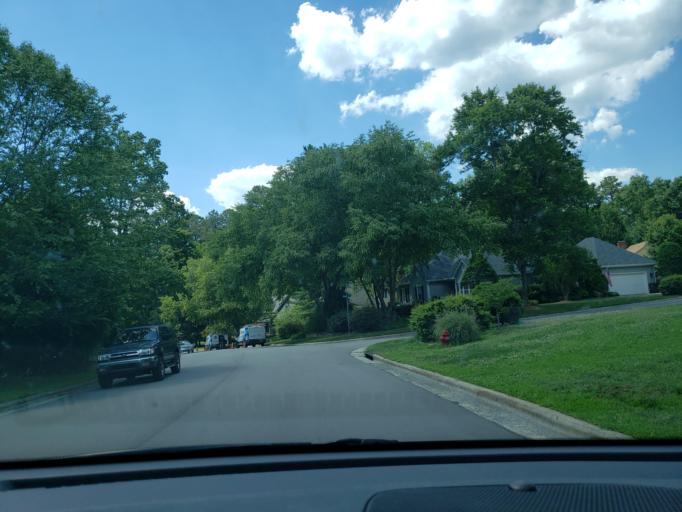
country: US
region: North Carolina
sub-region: Durham County
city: Durham
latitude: 35.9695
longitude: -78.9815
